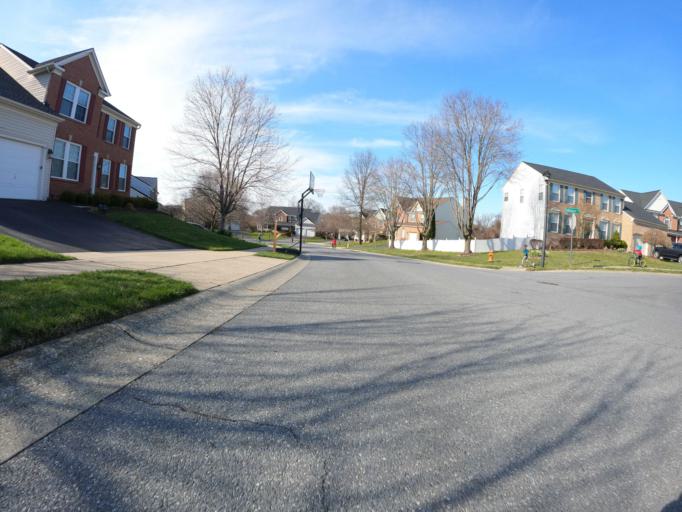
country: US
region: Maryland
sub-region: Howard County
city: Ellicott City
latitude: 39.3035
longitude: -76.8124
